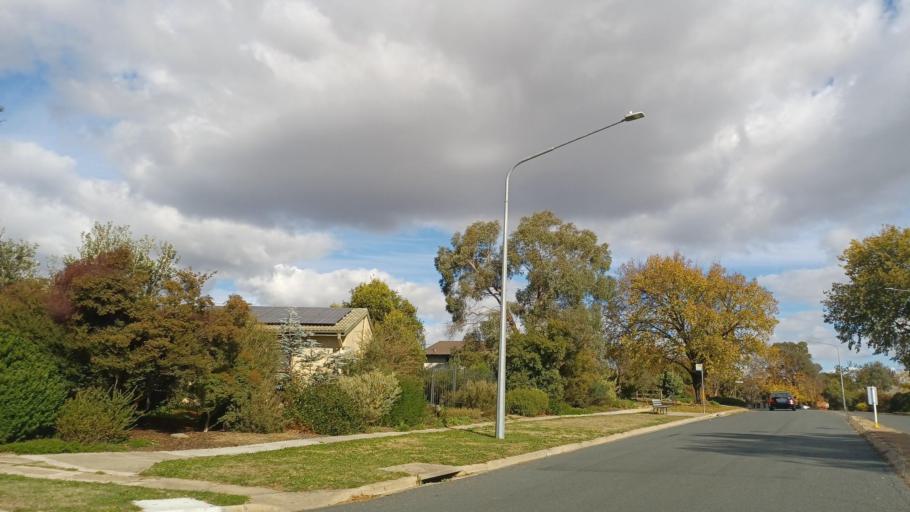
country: AU
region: Australian Capital Territory
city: Belconnen
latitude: -35.2099
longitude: 149.0907
